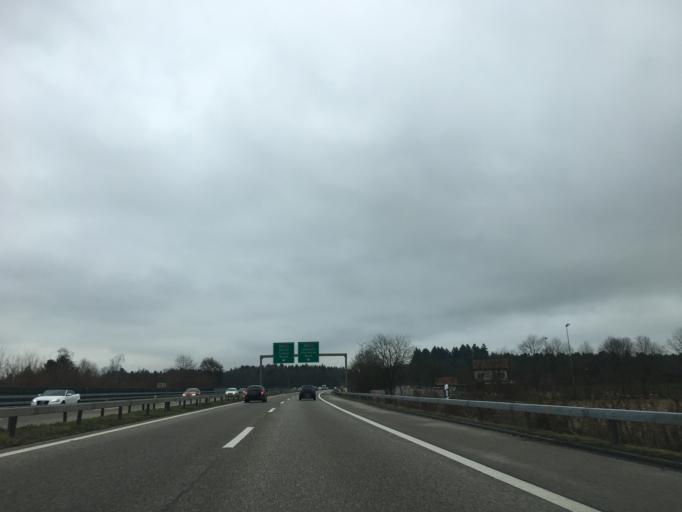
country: CH
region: Solothurn
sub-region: Bezirk Wasseramt
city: Luterbach
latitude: 47.2093
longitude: 7.5843
